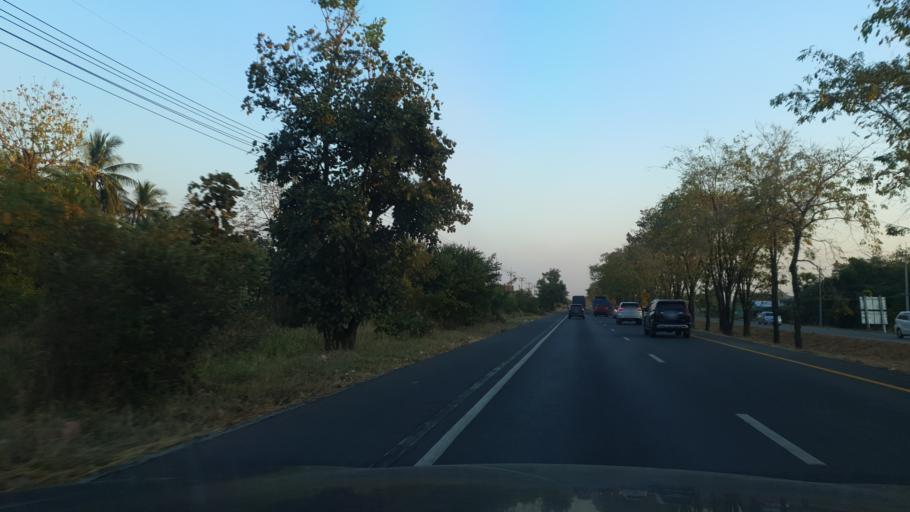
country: TH
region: Nakhon Sawan
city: Banphot Phisai
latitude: 15.8276
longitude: 99.9365
